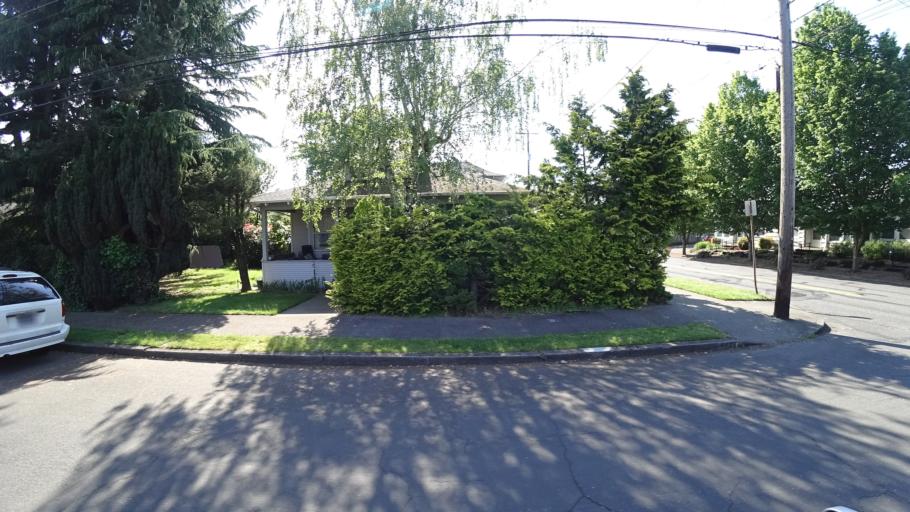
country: US
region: Oregon
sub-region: Multnomah County
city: Portland
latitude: 45.5553
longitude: -122.6429
